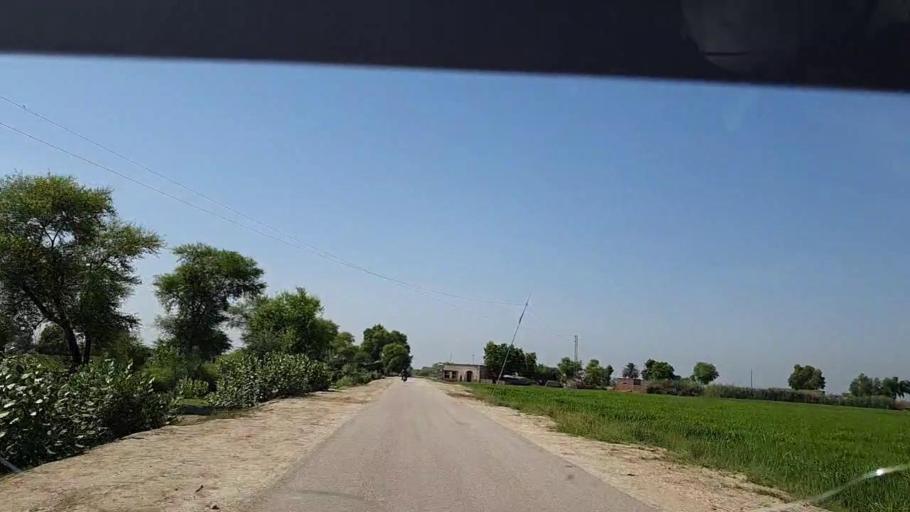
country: PK
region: Sindh
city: Kandhkot
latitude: 28.3072
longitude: 69.1091
